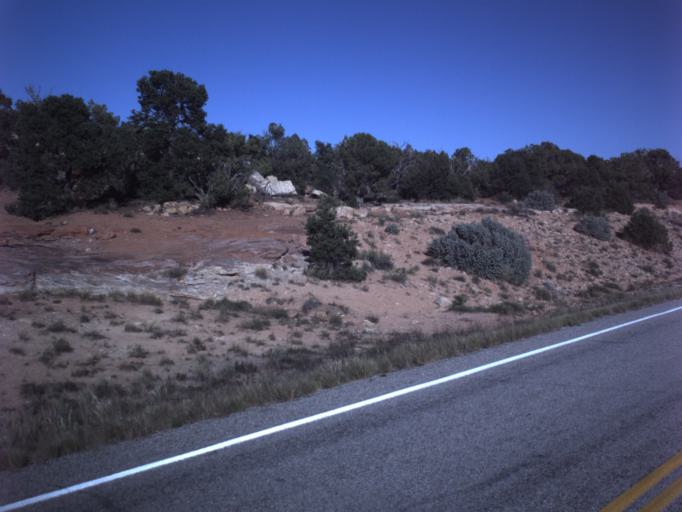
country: US
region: Utah
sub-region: San Juan County
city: Blanding
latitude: 37.5453
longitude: -109.7650
